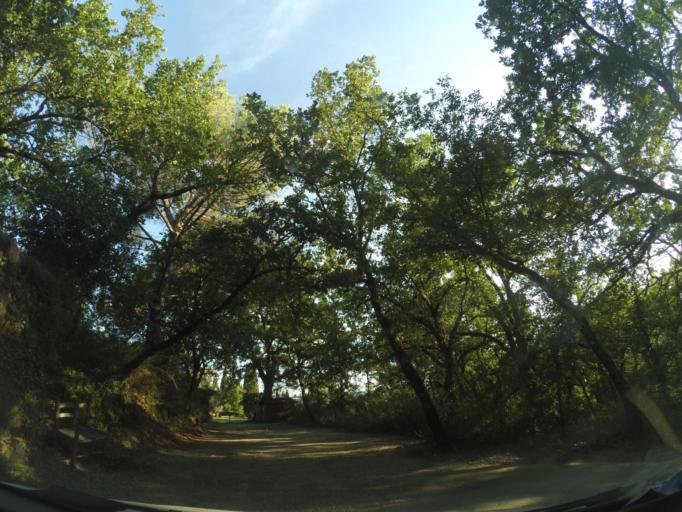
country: IT
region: Tuscany
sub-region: Province of Arezzo
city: Castiglion Fibocchi
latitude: 43.5300
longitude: 11.7803
